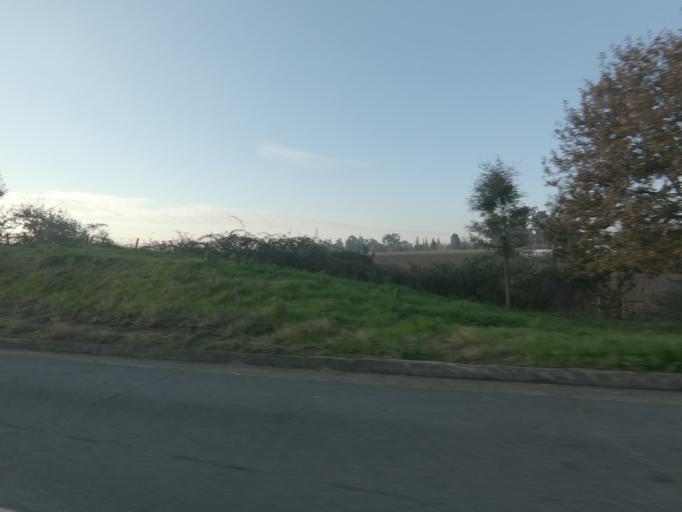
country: PT
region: Porto
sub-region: Penafiel
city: Penafiel
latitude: 41.2032
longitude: -8.3025
